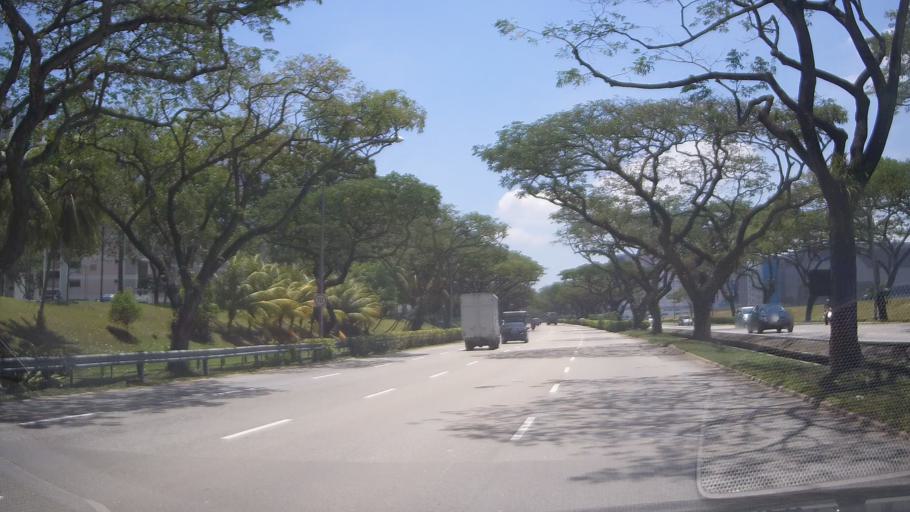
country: MY
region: Johor
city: Johor Bahru
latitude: 1.3541
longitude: 103.7158
